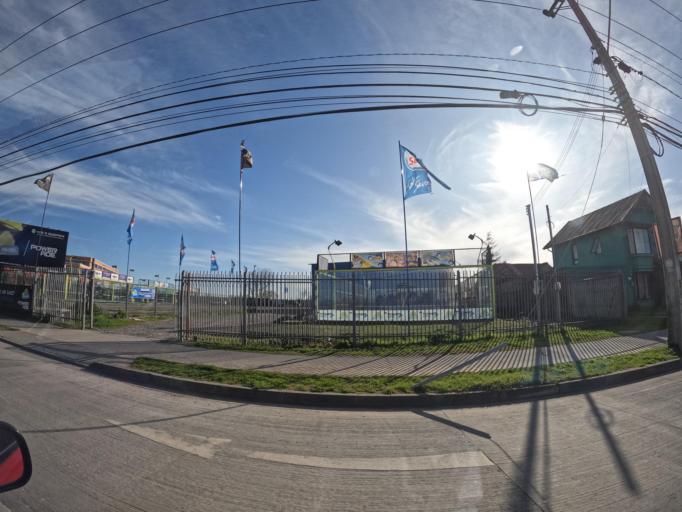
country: CL
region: Biobio
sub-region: Provincia de Concepcion
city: Concepcion
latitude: -36.7765
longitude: -73.0757
